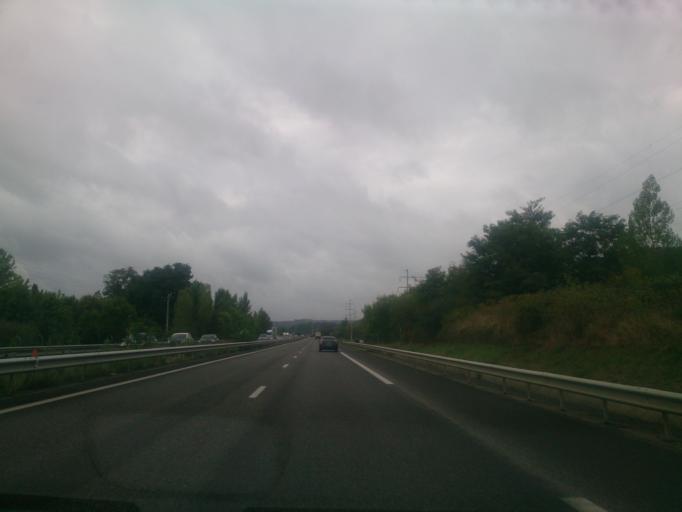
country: FR
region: Midi-Pyrenees
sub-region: Departement de la Haute-Garonne
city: Martres-Tolosane
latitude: 43.1949
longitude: 0.9920
